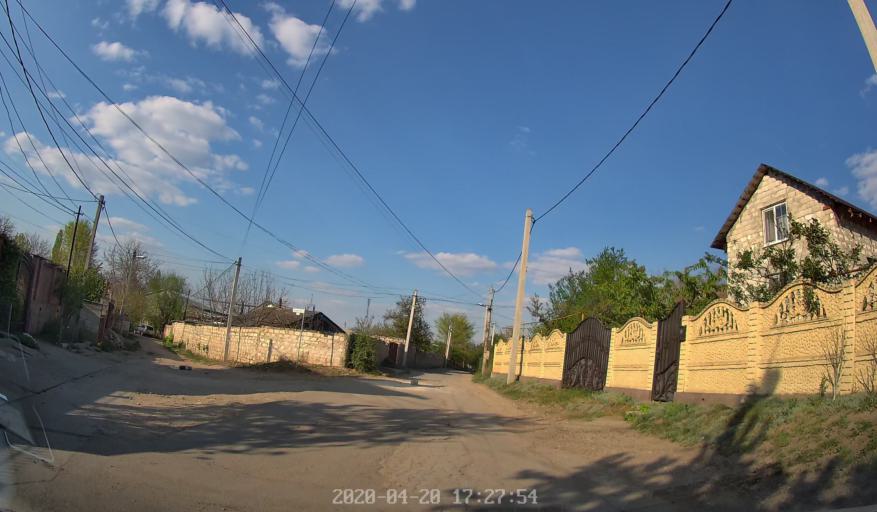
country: MD
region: Chisinau
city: Chisinau
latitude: 46.9943
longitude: 28.8720
